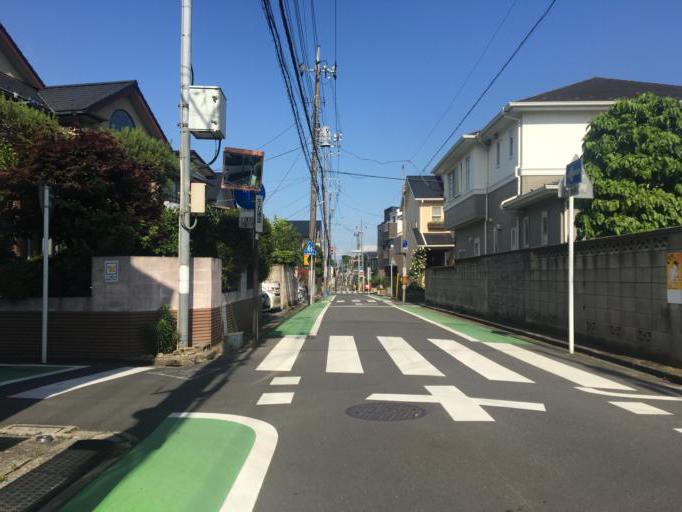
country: JP
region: Saitama
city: Yono
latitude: 35.8505
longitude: 139.6476
